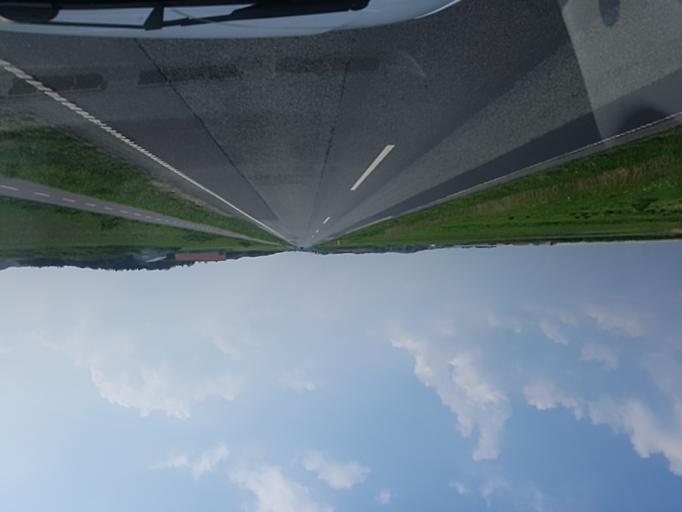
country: DK
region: Central Jutland
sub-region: Ringkobing-Skjern Kommune
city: Hvide Sande
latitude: 55.9665
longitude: 8.1452
